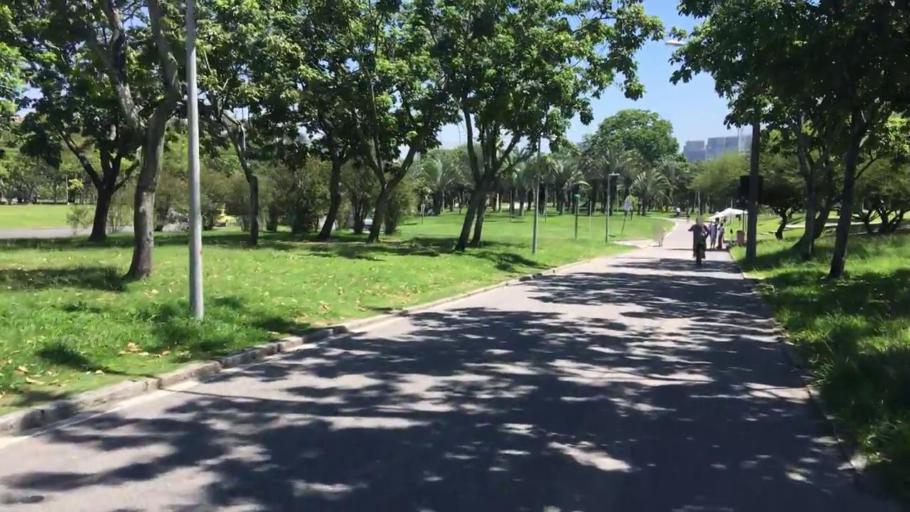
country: BR
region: Rio de Janeiro
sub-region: Rio De Janeiro
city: Rio de Janeiro
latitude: -22.9209
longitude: -43.1710
